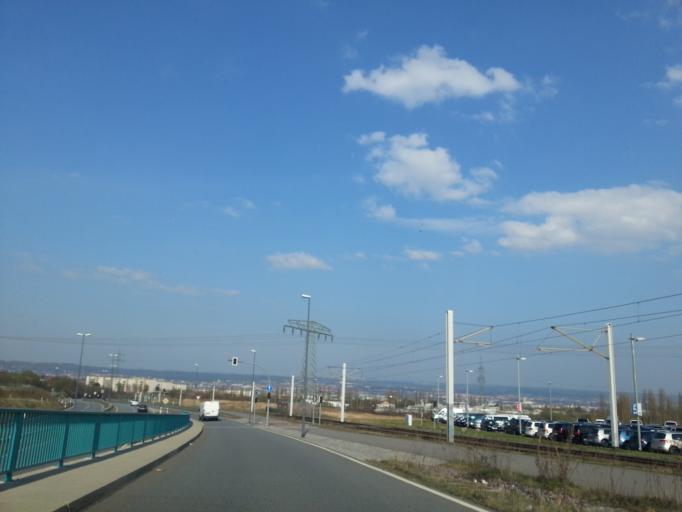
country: DE
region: Saxony
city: Freital
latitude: 51.0413
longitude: 13.6478
